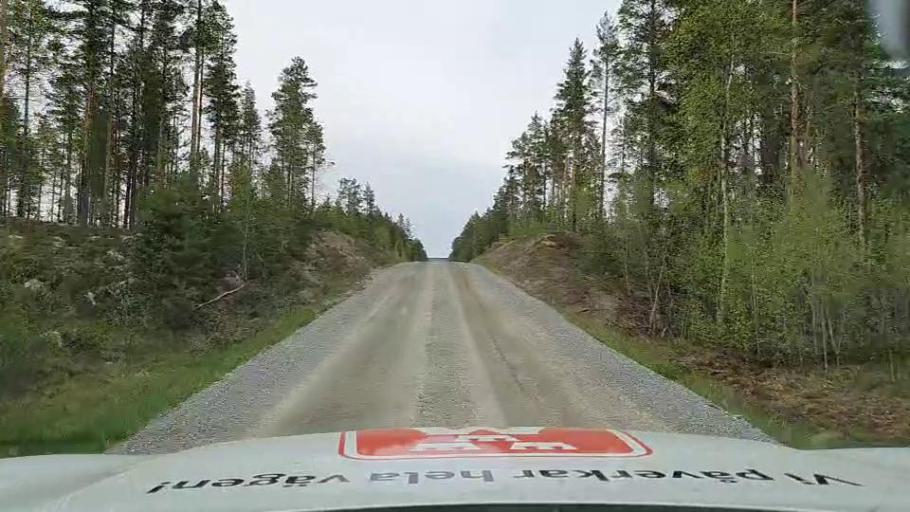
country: SE
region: Jaemtland
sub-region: Braecke Kommun
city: Braecke
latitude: 62.4756
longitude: 14.9166
